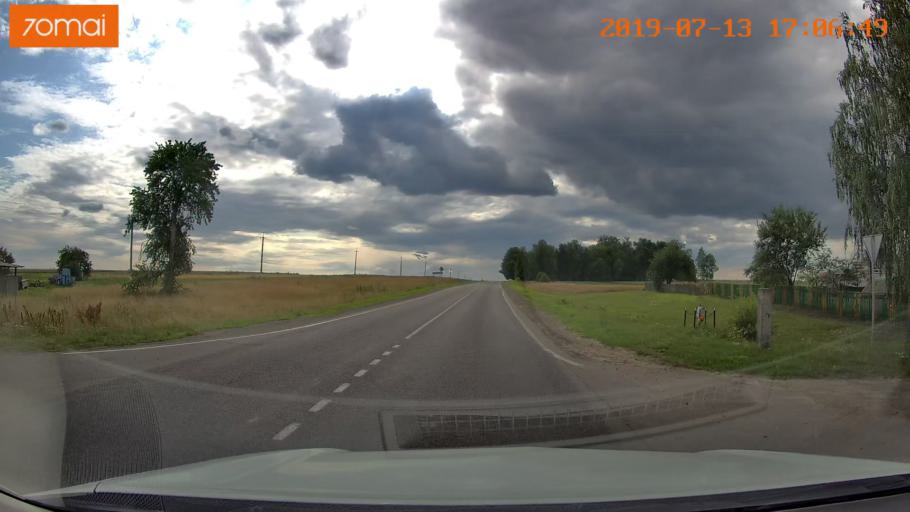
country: BY
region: Mogilev
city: Kirawsk
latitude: 53.2679
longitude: 29.3444
